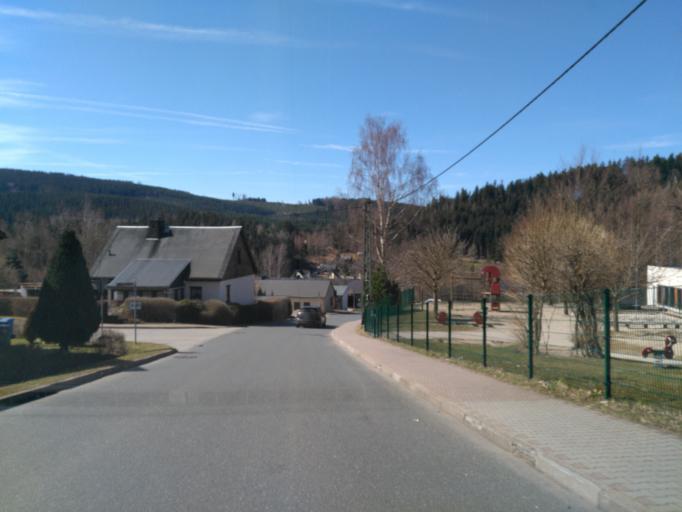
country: DE
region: Saxony
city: Breitenbrunn
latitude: 50.4789
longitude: 12.7497
